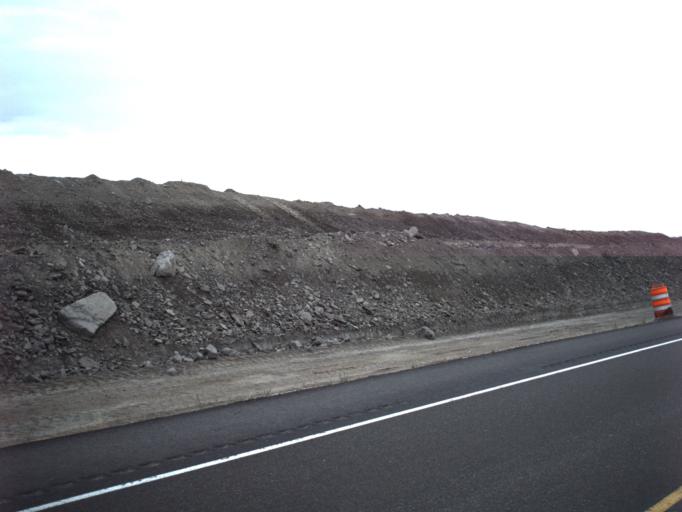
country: US
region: Utah
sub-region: Carbon County
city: East Carbon City
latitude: 39.0330
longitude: -110.3050
